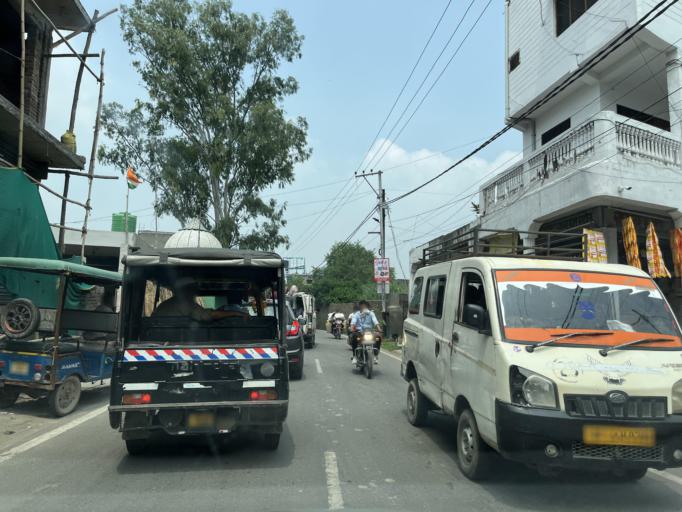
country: IN
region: Uttar Pradesh
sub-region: Bijnor
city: Najibabad
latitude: 29.6075
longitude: 78.3371
